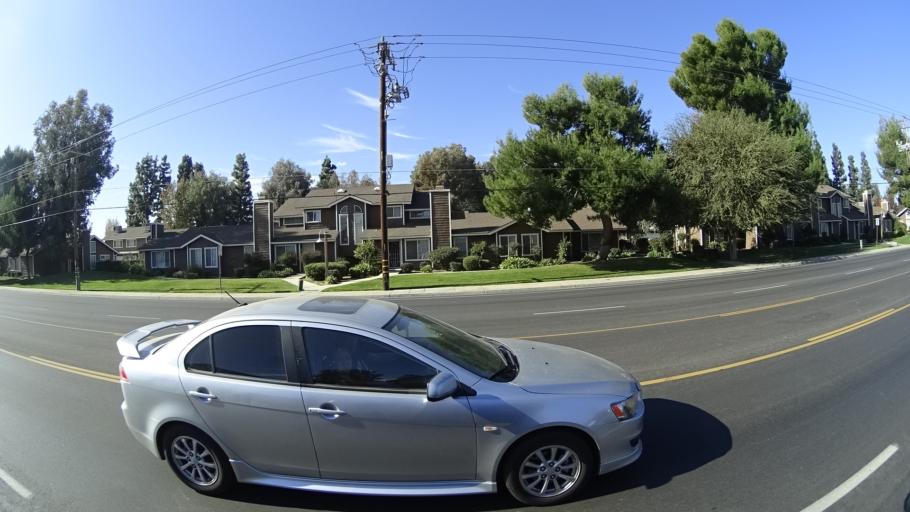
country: US
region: California
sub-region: Kern County
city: Greenacres
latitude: 35.3314
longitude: -119.0744
